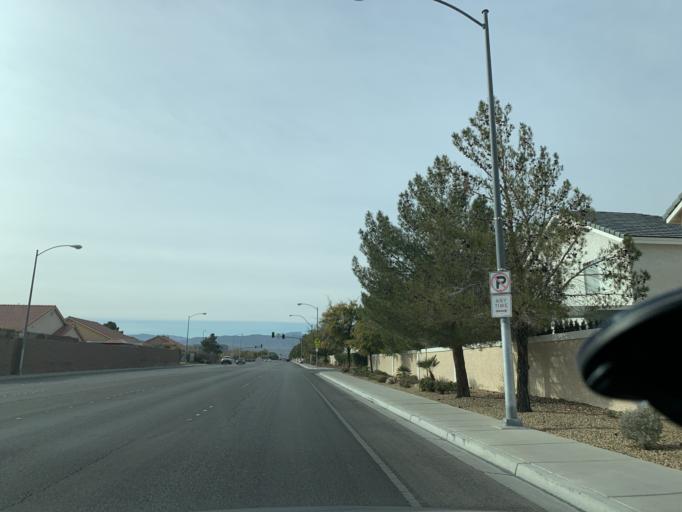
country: US
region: Nevada
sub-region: Clark County
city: Spring Valley
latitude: 36.0926
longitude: -115.2366
